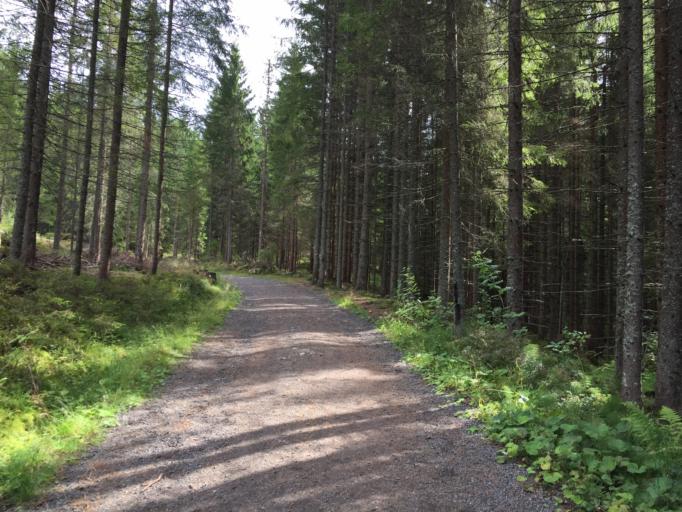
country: NO
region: Akershus
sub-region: Raelingen
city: Fjerdingby
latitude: 59.9166
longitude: 11.0148
